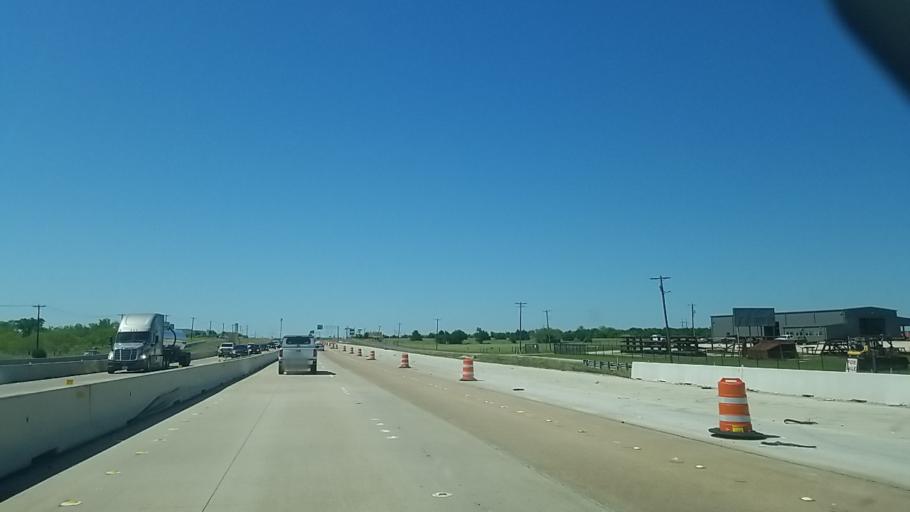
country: US
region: Texas
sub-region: Navarro County
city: Corsicana
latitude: 32.0511
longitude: -96.4495
